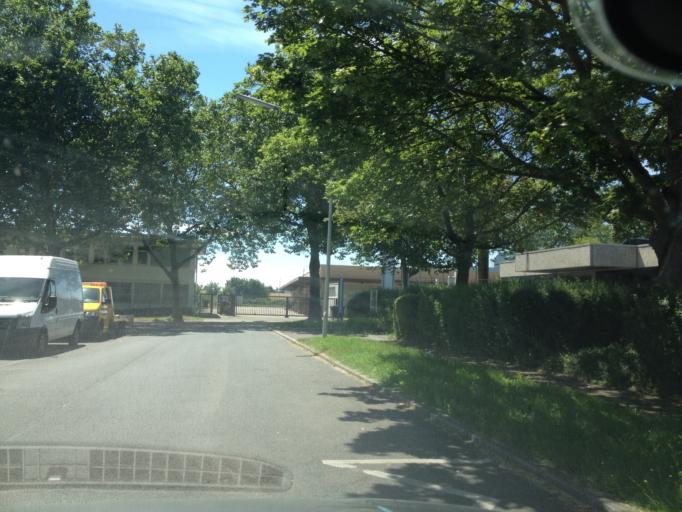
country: DE
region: Baden-Wuerttemberg
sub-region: Regierungsbezirk Stuttgart
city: Leingarten
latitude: 49.1418
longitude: 9.1620
